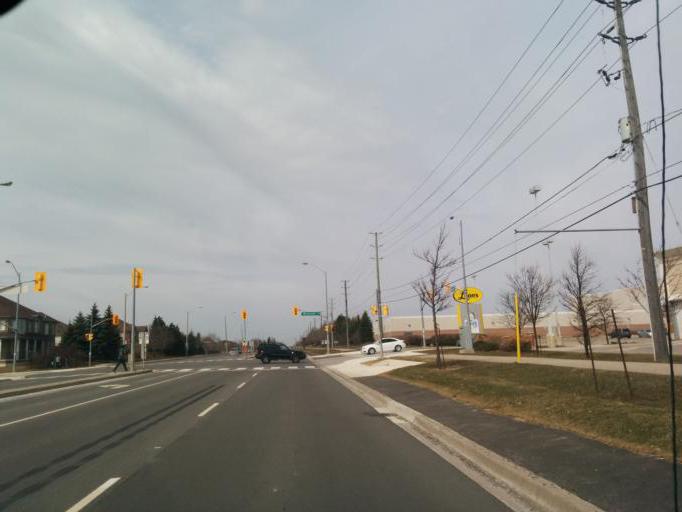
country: CA
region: Ontario
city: Brampton
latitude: 43.6976
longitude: -79.7996
